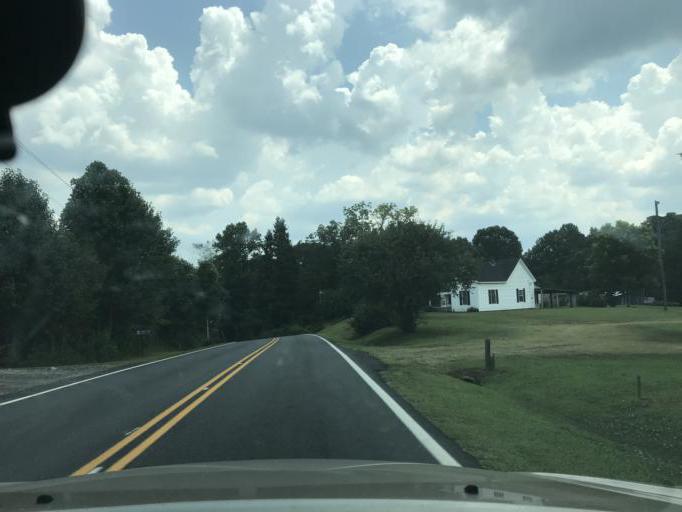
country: US
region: Georgia
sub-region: Forsyth County
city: Cumming
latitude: 34.2301
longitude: -84.2031
